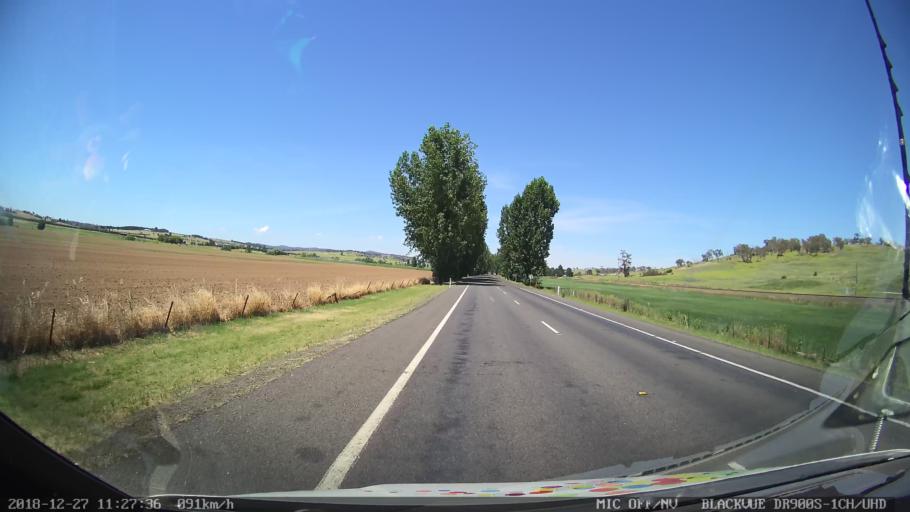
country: AU
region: New South Wales
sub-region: Bathurst Regional
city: Perthville
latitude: -33.4669
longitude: 149.5694
